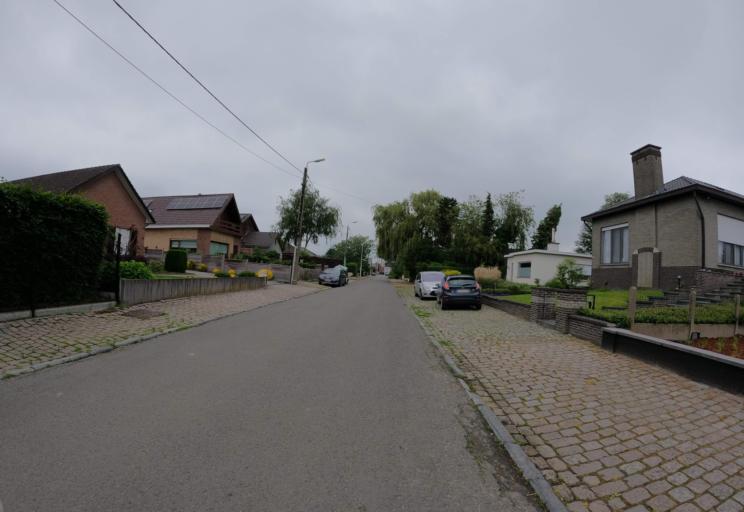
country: BE
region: Flanders
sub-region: Provincie Oost-Vlaanderen
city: Dendermonde
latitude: 51.0559
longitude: 4.1189
